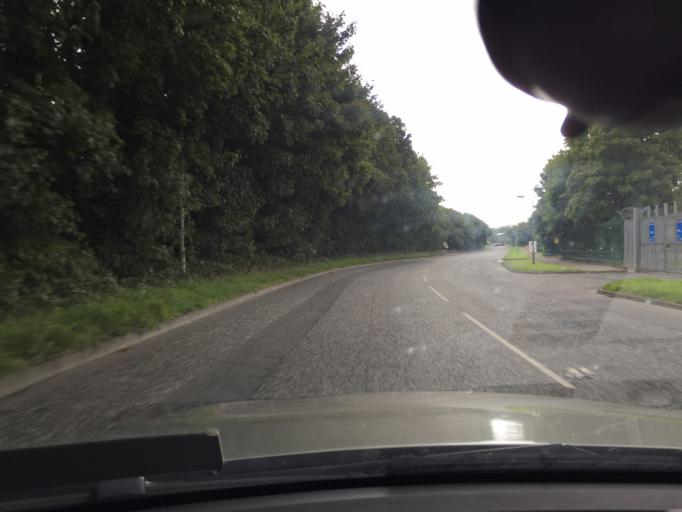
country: GB
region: Northern Ireland
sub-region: Newry and Mourne District
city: Newry
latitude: 54.1978
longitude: -6.3487
